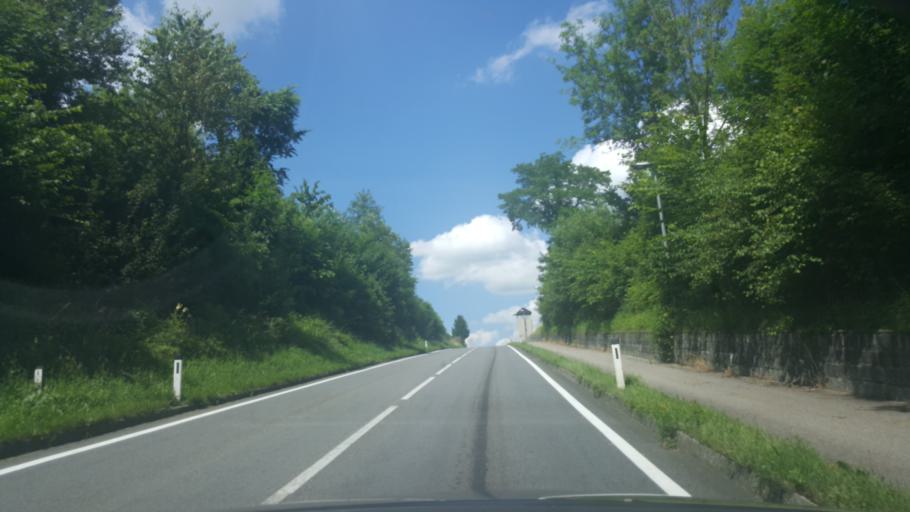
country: AT
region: Upper Austria
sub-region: Politischer Bezirk Vocklabruck
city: Gampern
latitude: 47.9988
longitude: 13.5449
